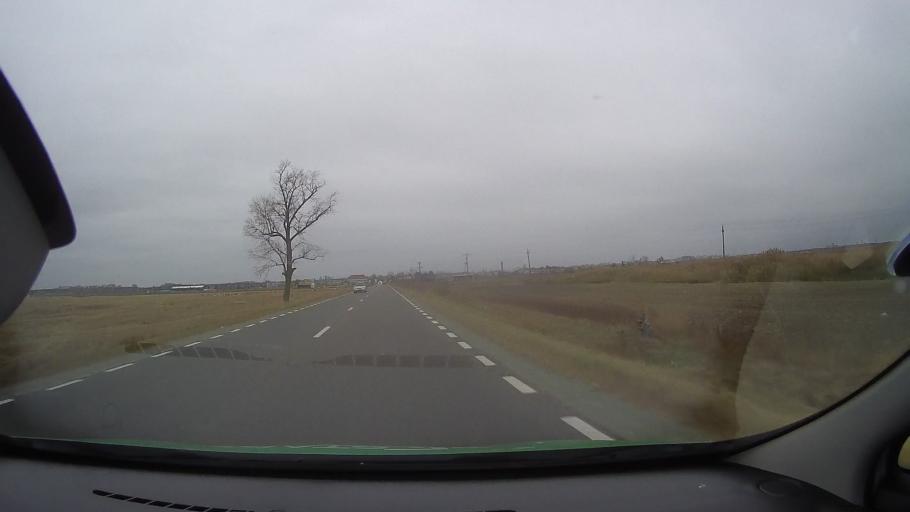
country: RO
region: Ialomita
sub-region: Comuna Slobozia
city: Slobozia
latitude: 44.5863
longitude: 27.3892
